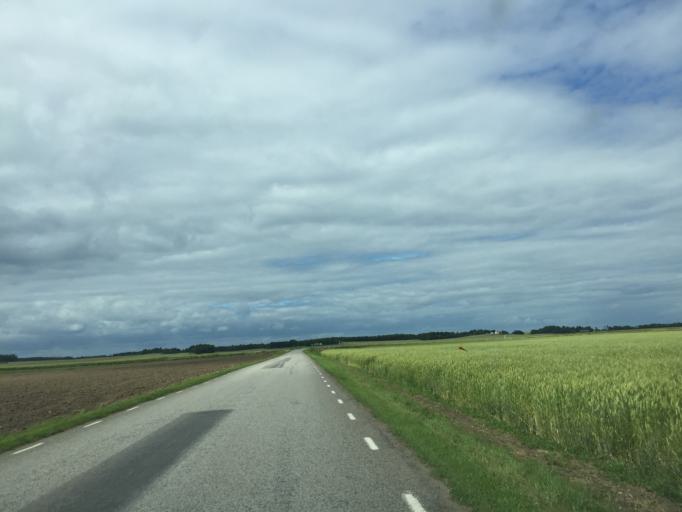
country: SE
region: OEstergoetland
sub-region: Vadstena Kommun
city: Vadstena
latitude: 58.4486
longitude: 14.8388
